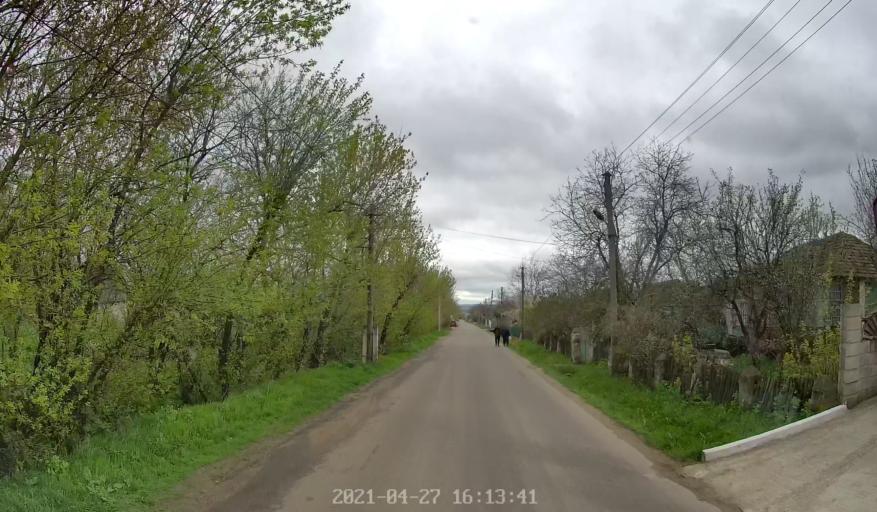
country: MD
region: Chisinau
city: Singera
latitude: 47.0075
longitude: 29.0132
